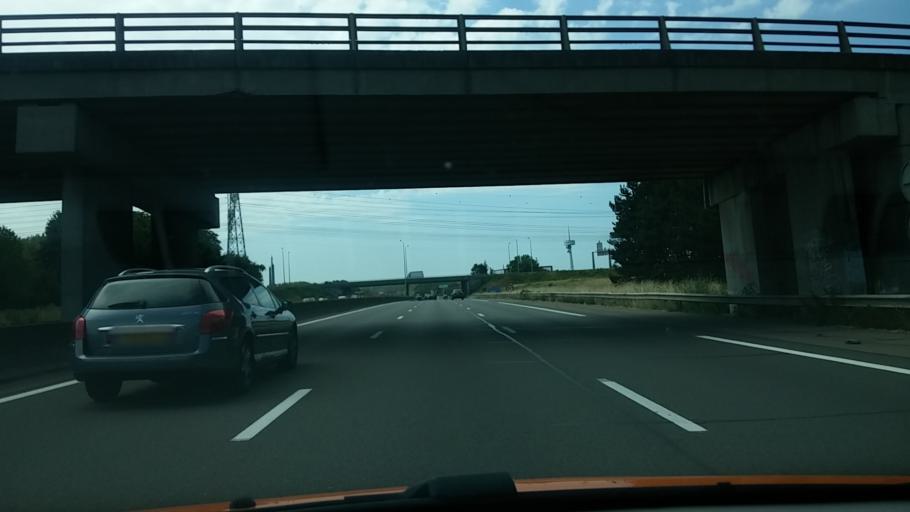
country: FR
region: Ile-de-France
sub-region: Departement de Seine-et-Marne
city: Croissy-Beaubourg
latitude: 48.8322
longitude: 2.6700
